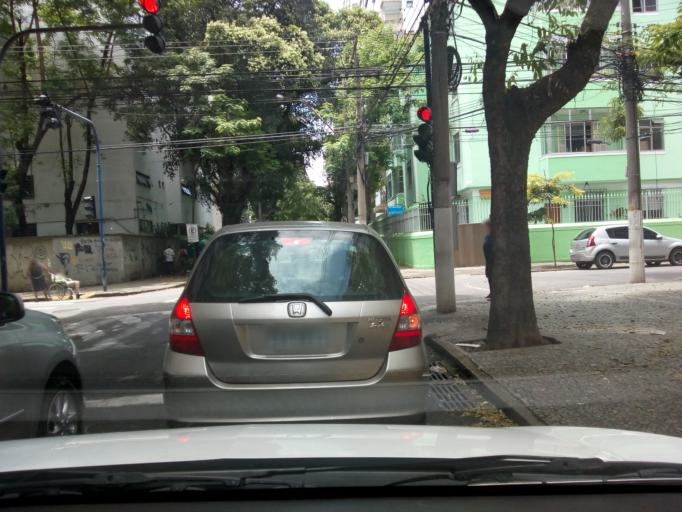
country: BR
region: Rio de Janeiro
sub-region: Niteroi
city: Niteroi
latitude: -22.9062
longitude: -43.1062
